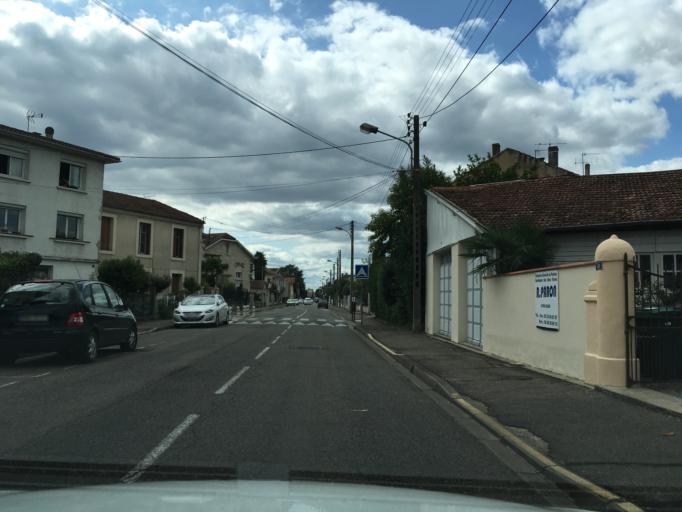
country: FR
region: Aquitaine
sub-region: Departement du Lot-et-Garonne
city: Agen
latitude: 44.1990
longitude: 0.6348
